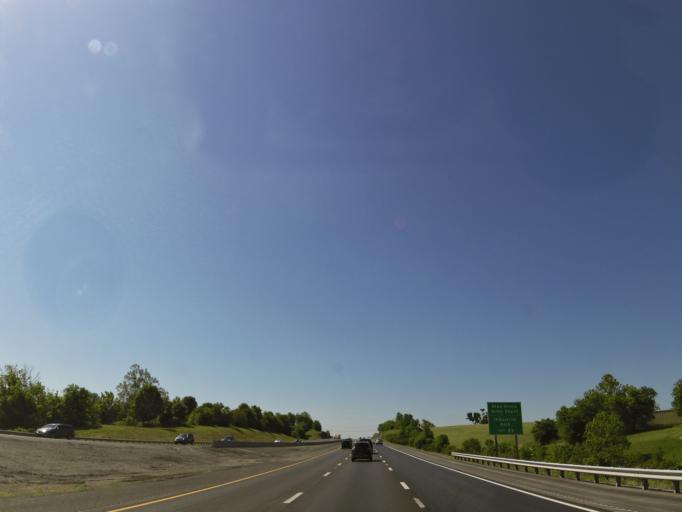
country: US
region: Kentucky
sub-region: Madison County
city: Richmond
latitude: 37.7065
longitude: -84.3193
